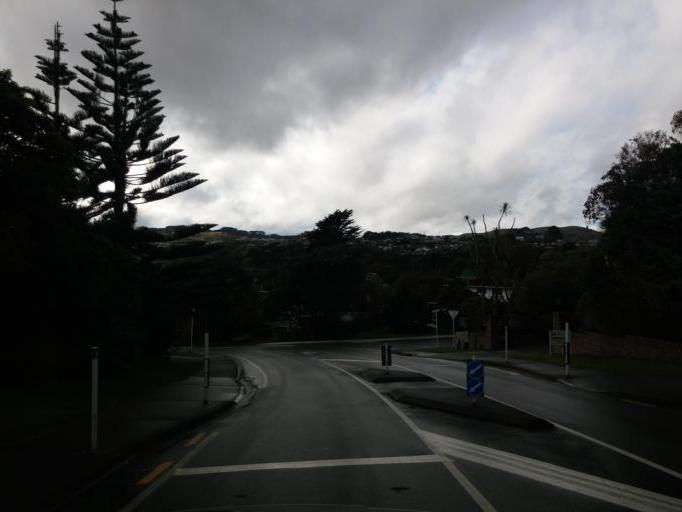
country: NZ
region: Wellington
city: Petone
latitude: -41.2073
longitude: 174.8073
